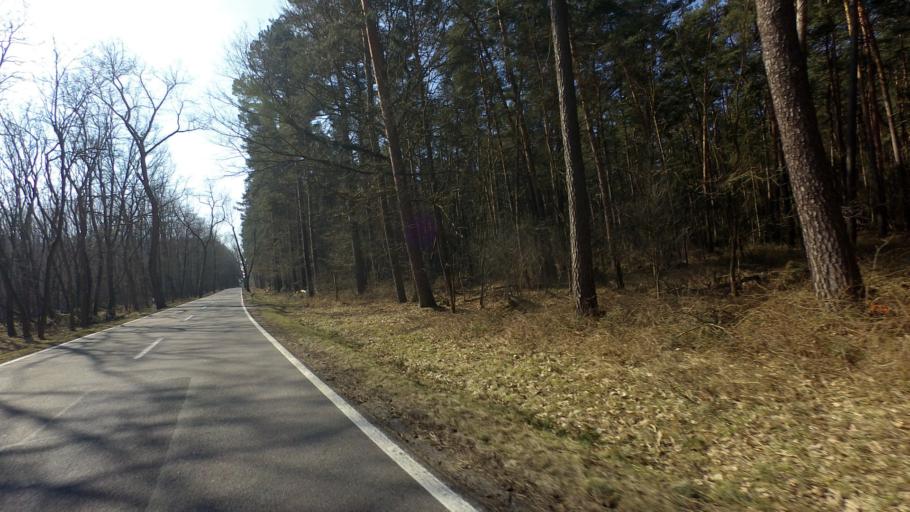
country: DE
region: Saxony-Anhalt
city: Nudersdorf
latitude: 51.9888
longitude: 12.5836
